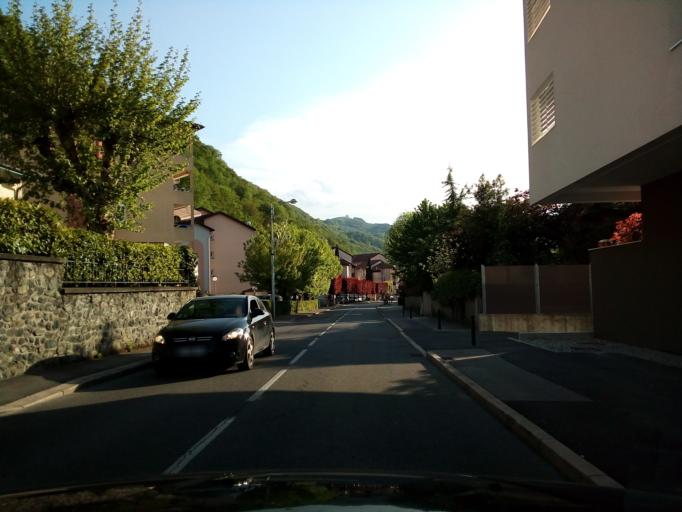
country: FR
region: Rhone-Alpes
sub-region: Departement de l'Isere
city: Domene
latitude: 45.1997
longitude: 5.8372
